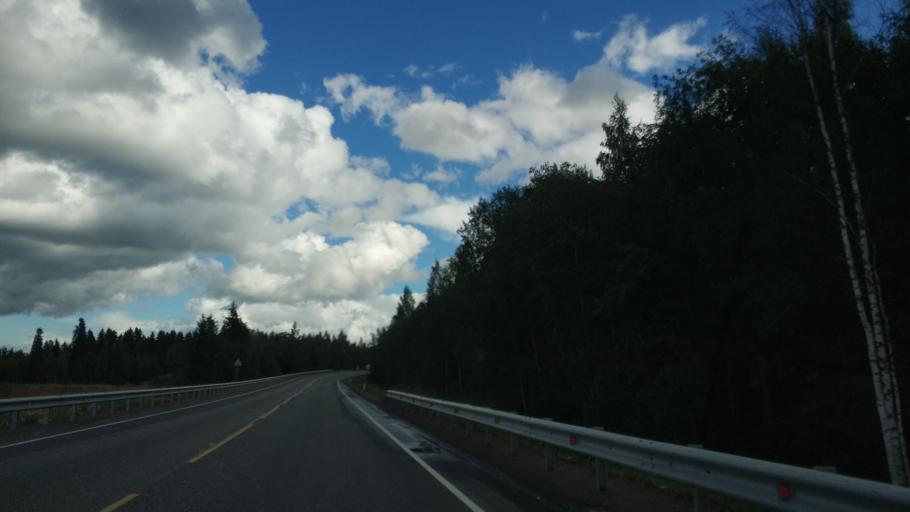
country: RU
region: Republic of Karelia
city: Khelyulya
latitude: 61.7851
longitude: 30.6453
